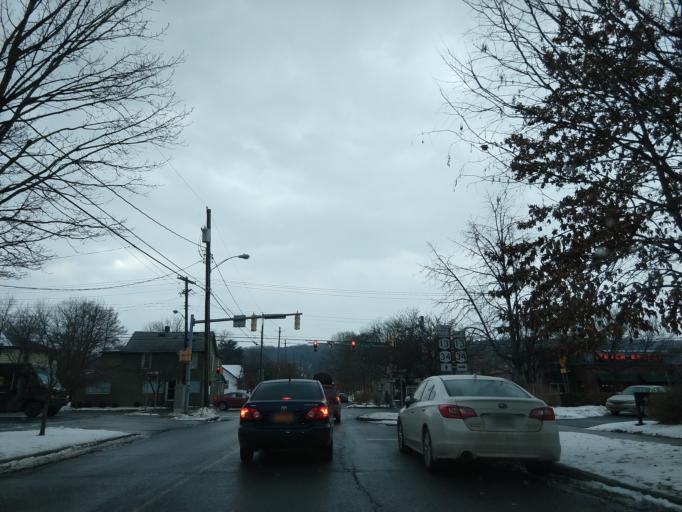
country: US
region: New York
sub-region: Tompkins County
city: Ithaca
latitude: 42.4424
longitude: -76.5081
